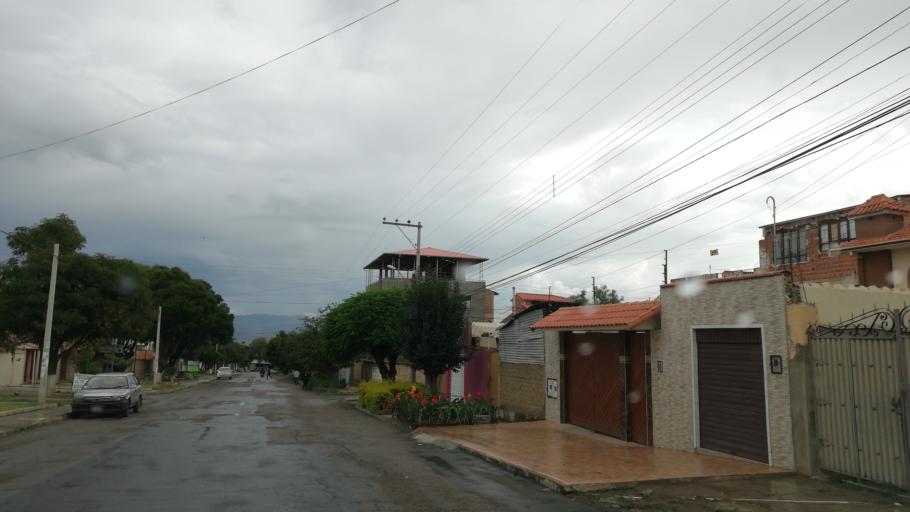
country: BO
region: Cochabamba
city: Cochabamba
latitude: -17.3509
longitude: -66.1803
